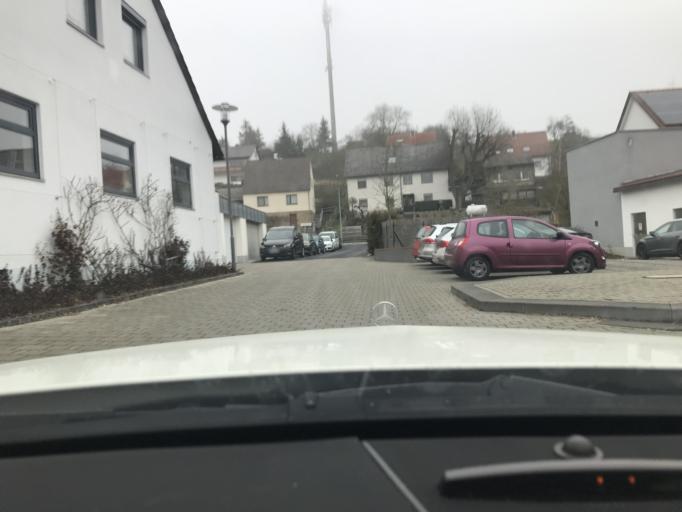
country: DE
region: Bavaria
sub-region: Regierungsbezirk Unterfranken
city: Werneck
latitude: 50.0016
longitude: 10.0666
